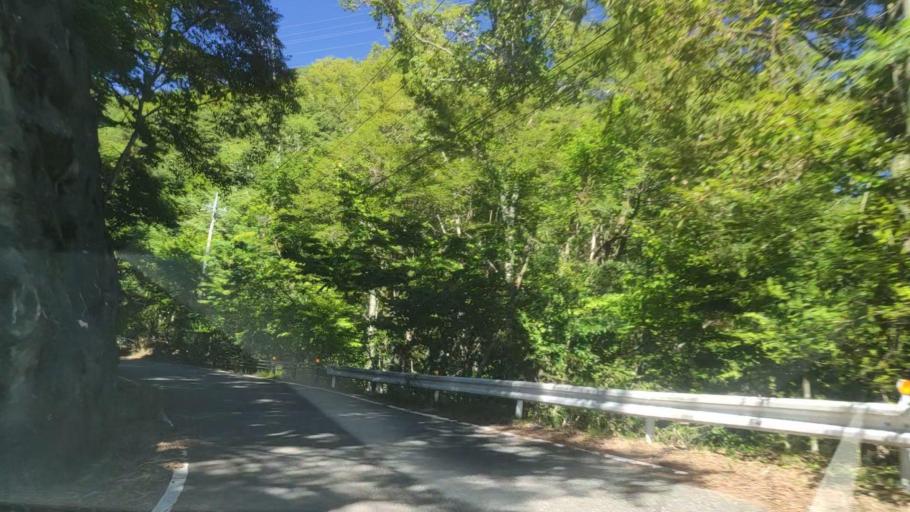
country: JP
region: Yamanashi
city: Fujikawaguchiko
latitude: 35.5494
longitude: 138.7772
